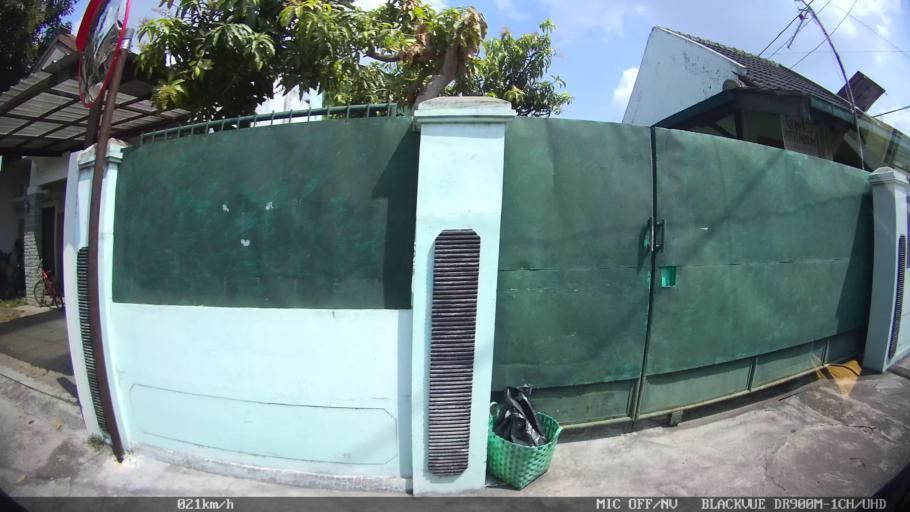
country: ID
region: Daerah Istimewa Yogyakarta
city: Yogyakarta
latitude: -7.8076
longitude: 110.4048
